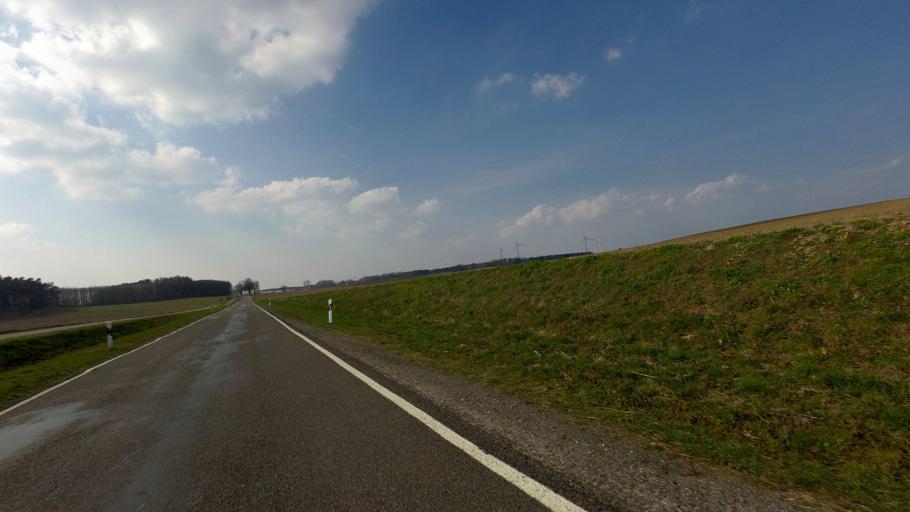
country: DE
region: Brandenburg
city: Ihlow
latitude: 51.9479
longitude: 13.3862
